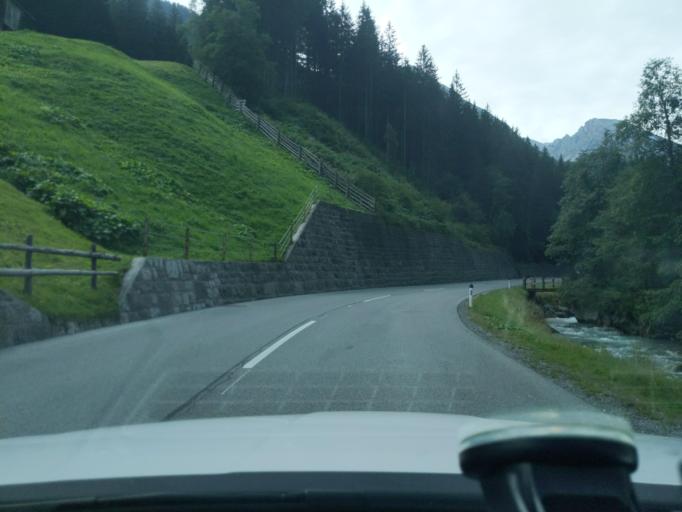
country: AT
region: Tyrol
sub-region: Politischer Bezirk Schwaz
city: Schwendau
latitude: 47.1470
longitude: 11.7206
